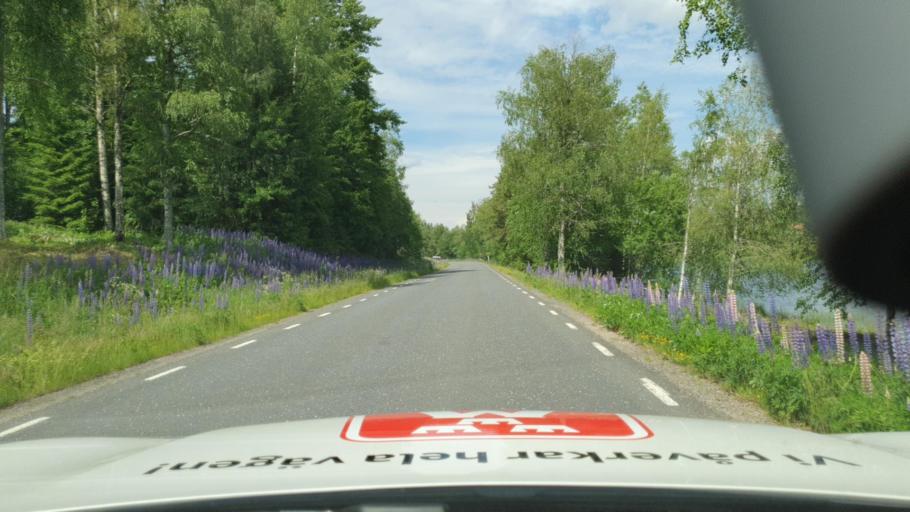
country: SE
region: Vaermland
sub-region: Torsby Kommun
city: Torsby
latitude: 60.6555
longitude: 12.7039
